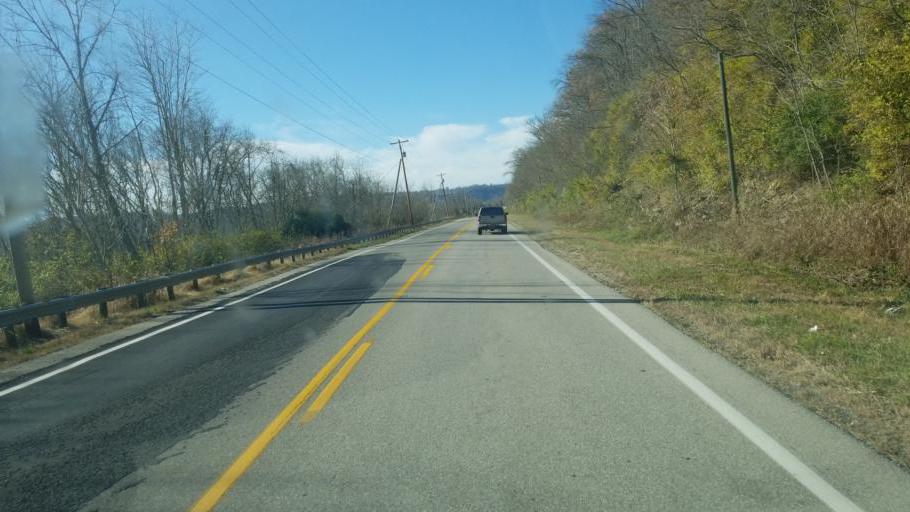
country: US
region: Kentucky
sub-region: Mason County
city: Maysville
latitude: 38.6489
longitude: -83.7283
